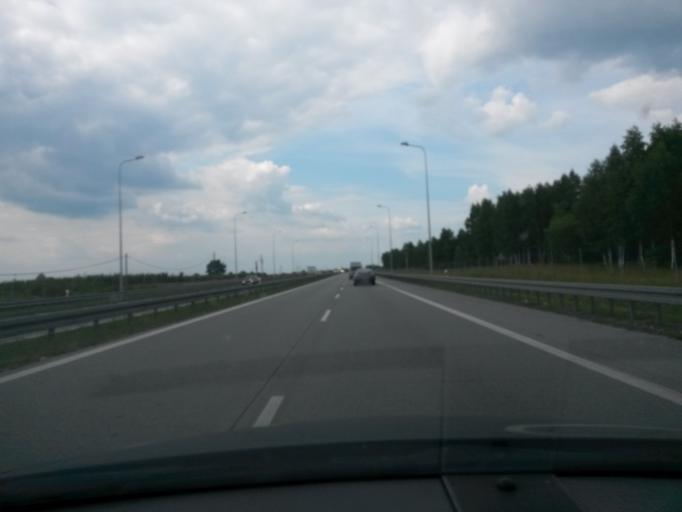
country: PL
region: Lodz Voivodeship
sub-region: Powiat skierniewicki
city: Kowiesy
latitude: 51.8684
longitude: 20.3850
